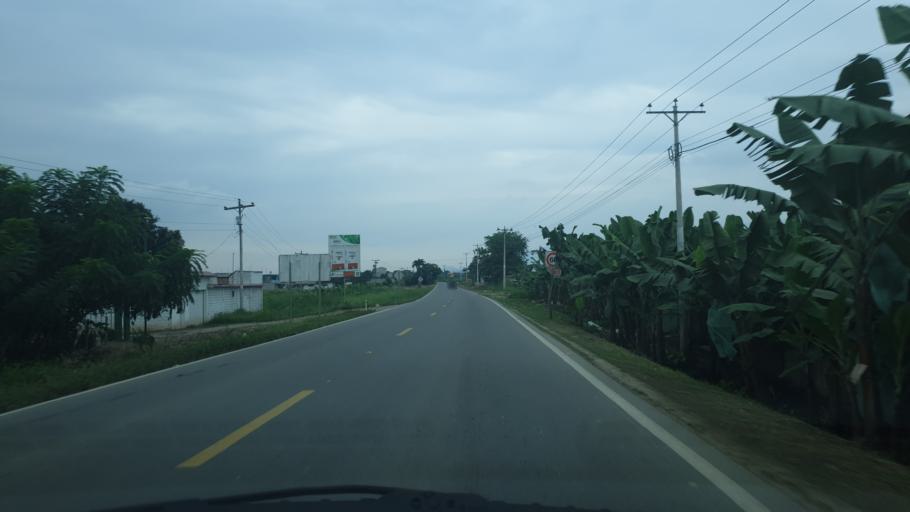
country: EC
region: El Oro
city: Pasaje
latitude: -3.3497
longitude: -79.8148
